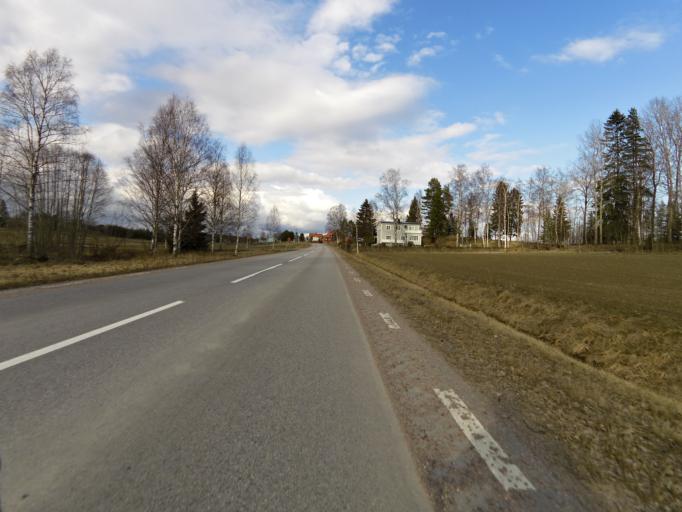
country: SE
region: Dalarna
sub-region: Avesta Kommun
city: Horndal
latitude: 60.4604
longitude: 16.4565
